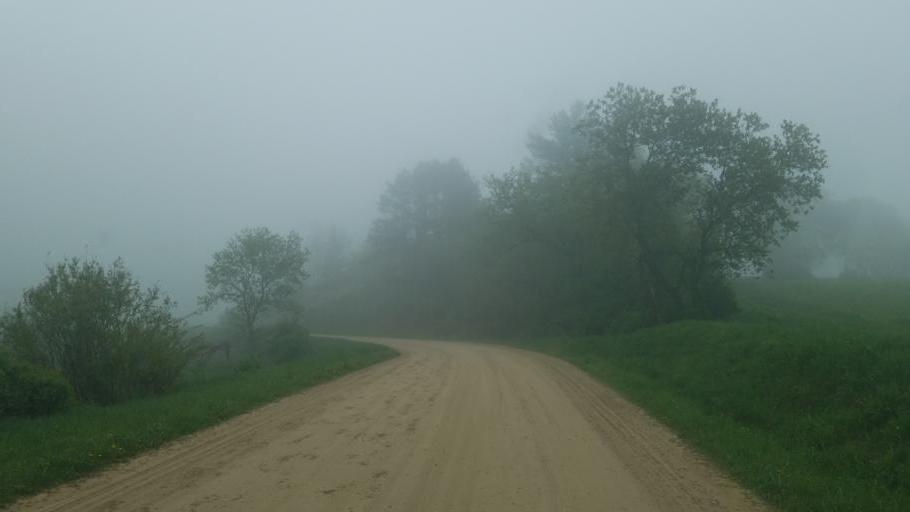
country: US
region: Wisconsin
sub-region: Vernon County
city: Hillsboro
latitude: 43.6311
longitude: -90.3479
